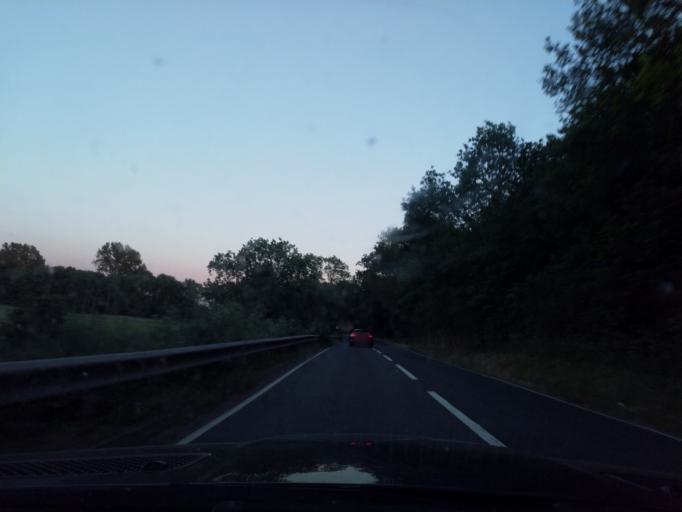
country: GB
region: England
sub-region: Solihull
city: Hampton in Arden
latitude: 52.4422
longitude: -1.6849
